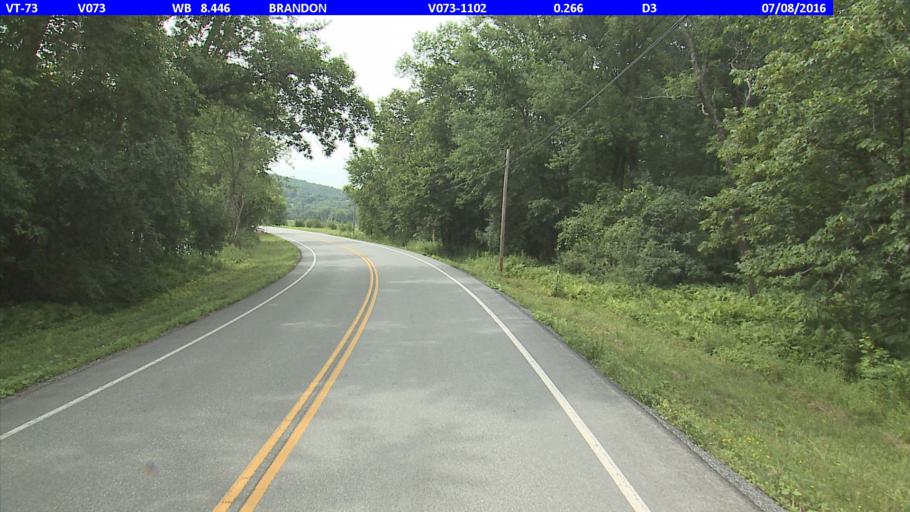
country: US
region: Vermont
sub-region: Rutland County
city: Brandon
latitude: 43.8066
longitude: -73.1416
